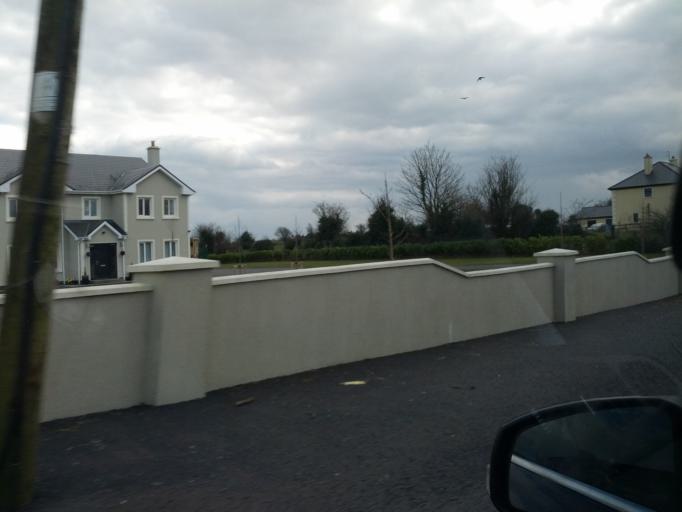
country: IE
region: Connaught
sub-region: County Galway
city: Athenry
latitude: 53.4838
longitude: -8.6317
